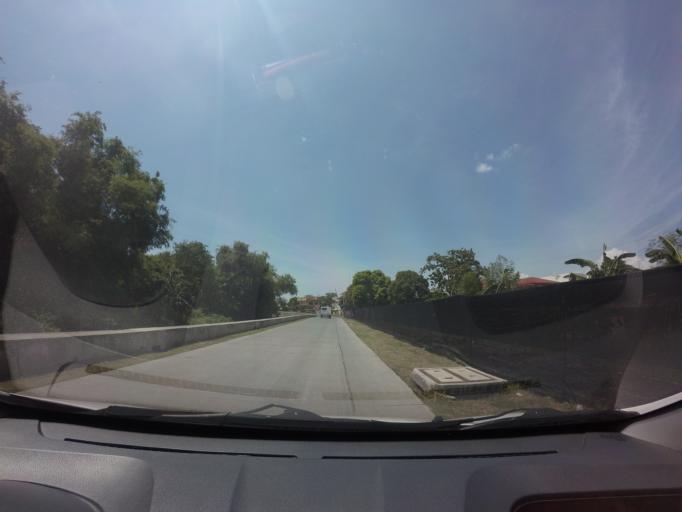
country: PH
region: Calabarzon
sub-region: Province of Rizal
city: Las Pinas
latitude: 14.4255
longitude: 120.9871
